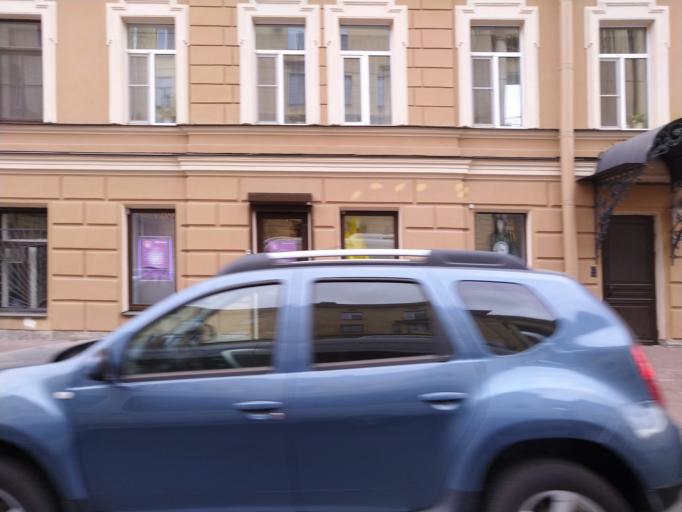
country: RU
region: St.-Petersburg
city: Centralniy
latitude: 59.9437
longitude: 30.3921
